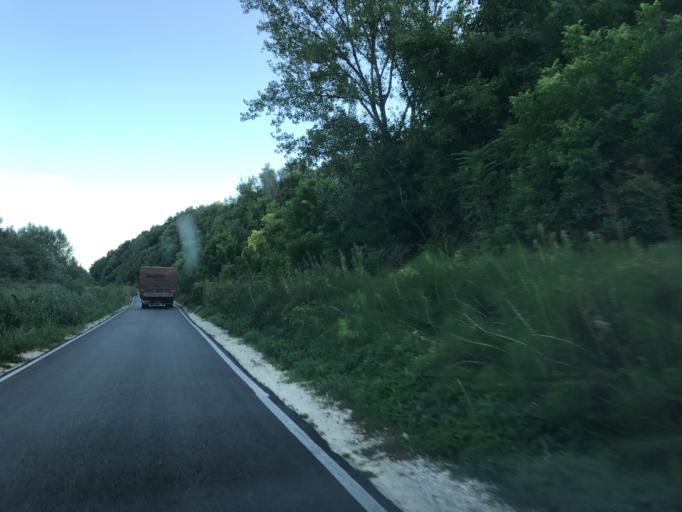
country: BG
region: Vidin
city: Bregovo
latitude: 44.1387
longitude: 22.6025
